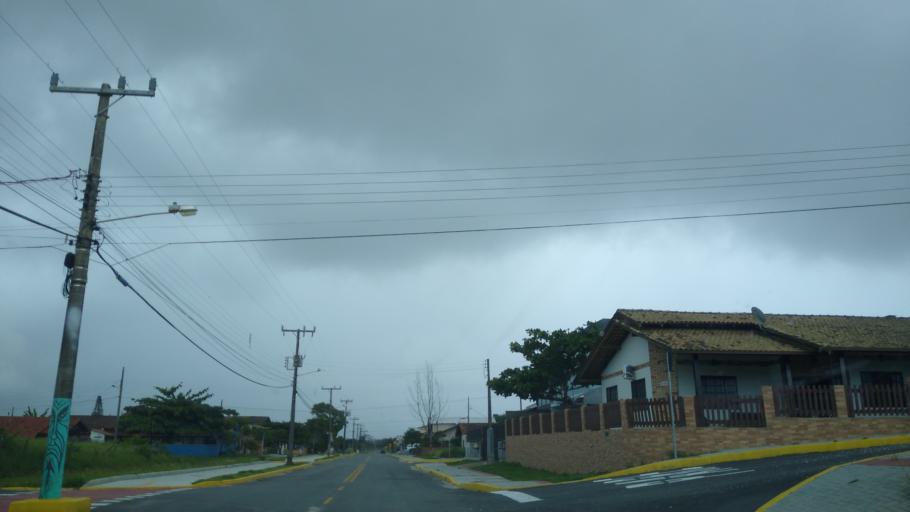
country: BR
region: Santa Catarina
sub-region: Sao Francisco Do Sul
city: Sao Francisco do Sul
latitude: -26.2380
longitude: -48.5093
